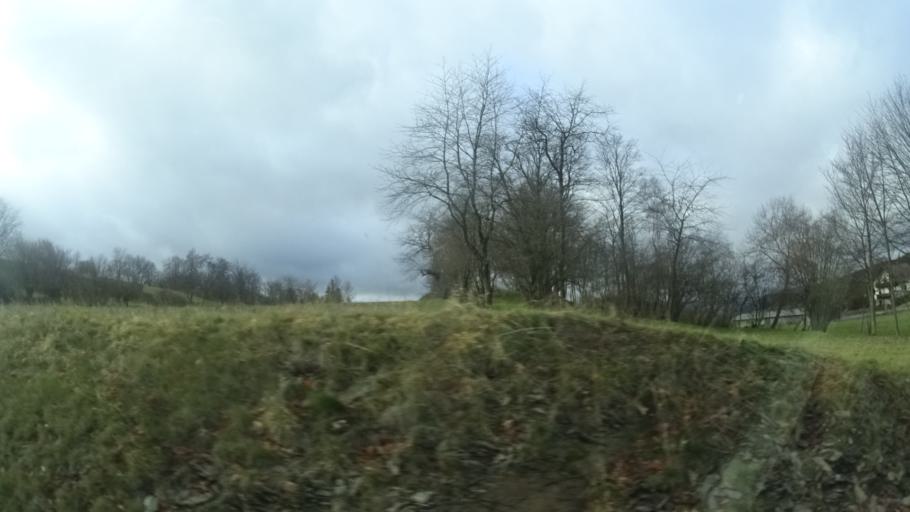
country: DE
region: Thuringia
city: Doschnitz
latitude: 50.6132
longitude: 11.2974
